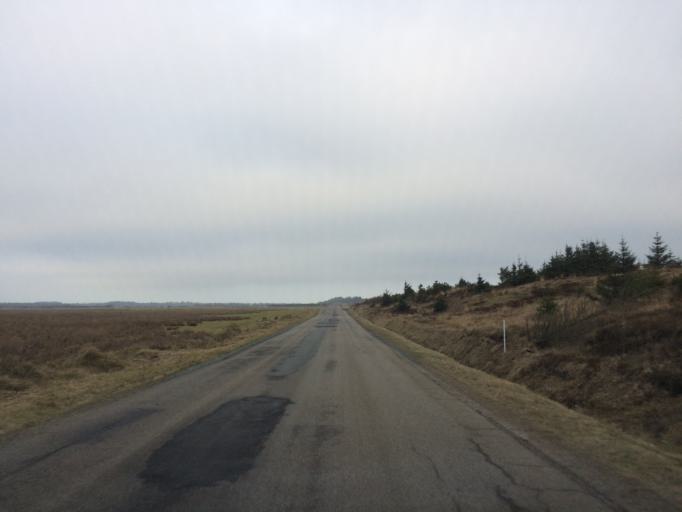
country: DK
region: South Denmark
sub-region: Varde Kommune
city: Oksbol
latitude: 55.6448
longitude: 8.1781
